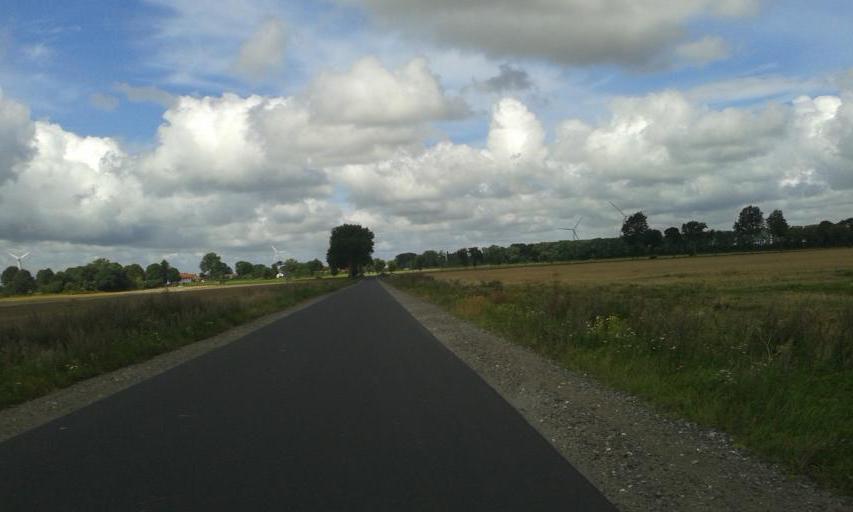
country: PL
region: West Pomeranian Voivodeship
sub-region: Powiat slawienski
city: Slawno
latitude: 54.3260
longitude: 16.5766
